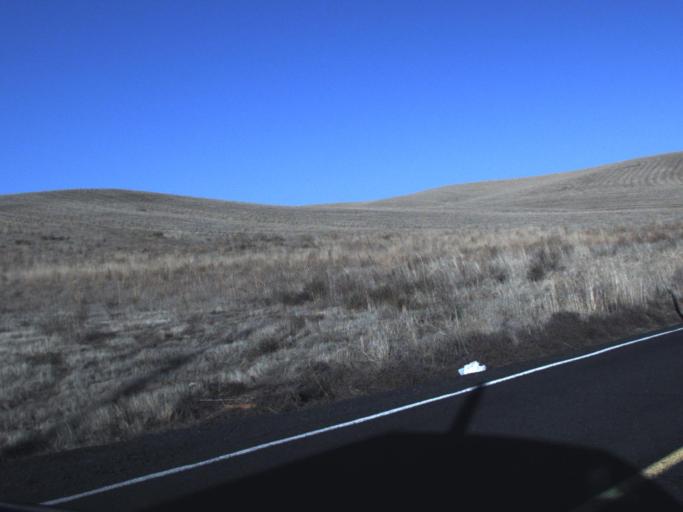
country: US
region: Washington
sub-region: Walla Walla County
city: Waitsburg
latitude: 46.6778
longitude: -118.3384
